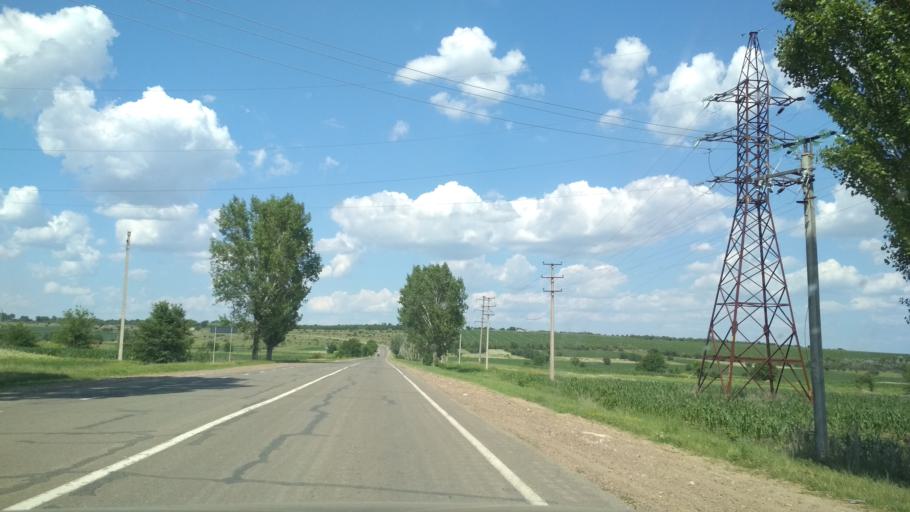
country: MD
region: Criuleni
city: Criuleni
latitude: 47.1529
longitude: 29.1543
